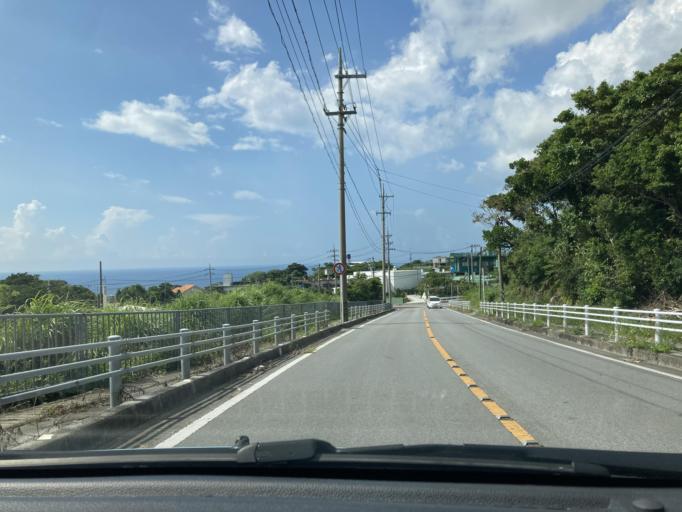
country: JP
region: Okinawa
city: Tomigusuku
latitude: 26.1470
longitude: 127.7915
